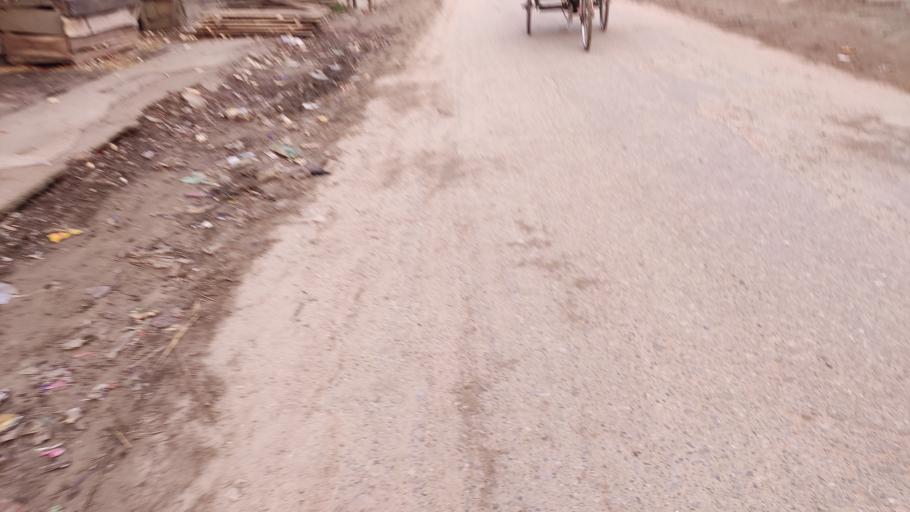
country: BD
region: Dhaka
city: Netrakona
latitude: 24.7167
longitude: 90.9504
